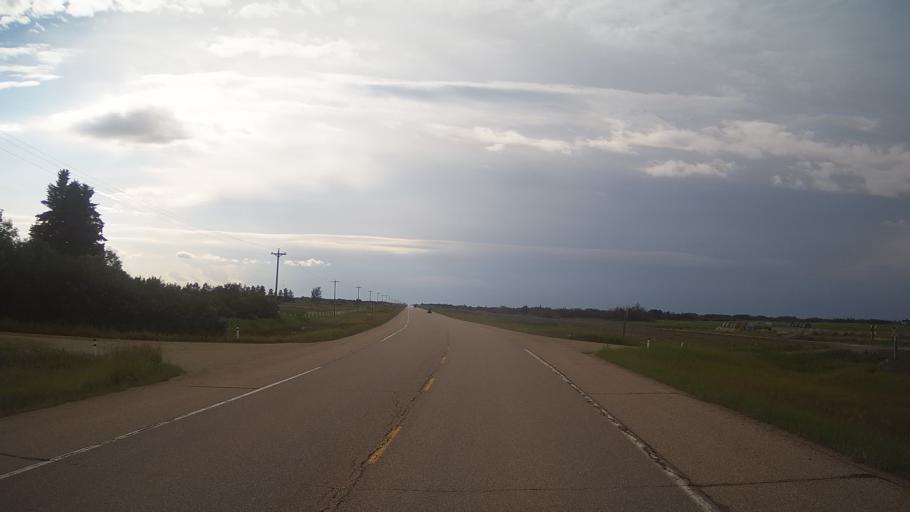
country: CA
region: Alberta
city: Viking
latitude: 53.1382
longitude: -111.9300
